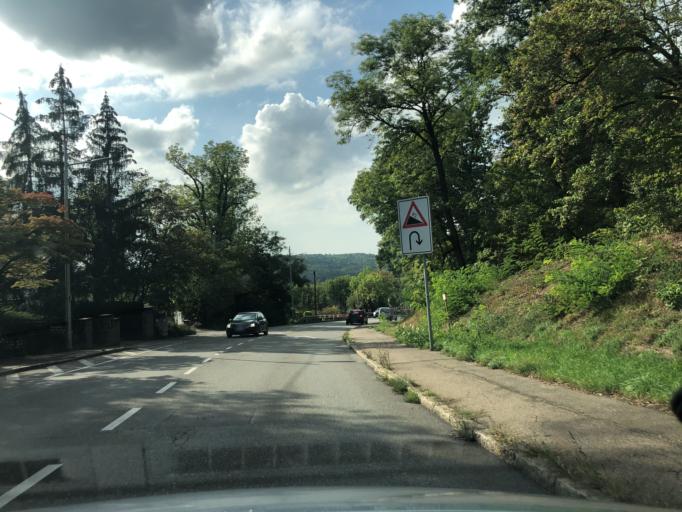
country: DE
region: Baden-Wuerttemberg
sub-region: Regierungsbezirk Stuttgart
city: Stuttgart
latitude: 48.7494
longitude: 9.1518
